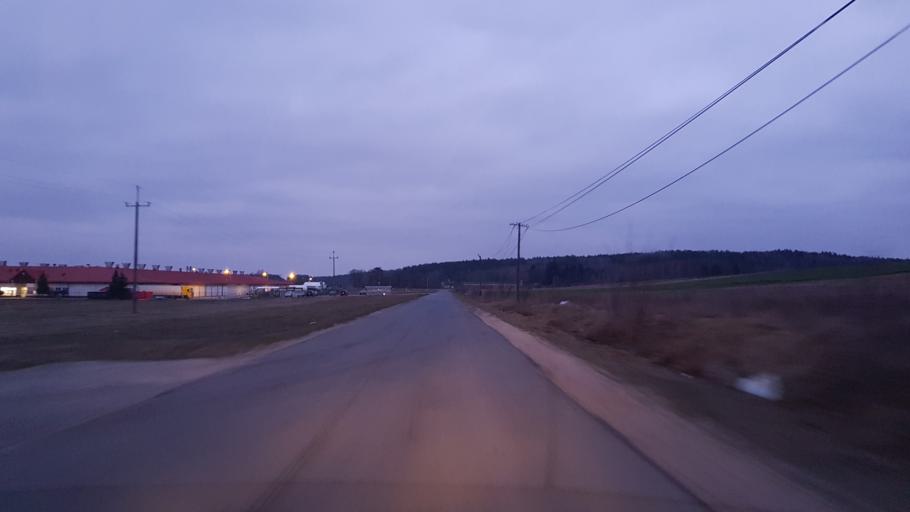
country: PL
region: Greater Poland Voivodeship
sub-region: Powiat zlotowski
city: Okonek
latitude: 53.5006
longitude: 16.8050
